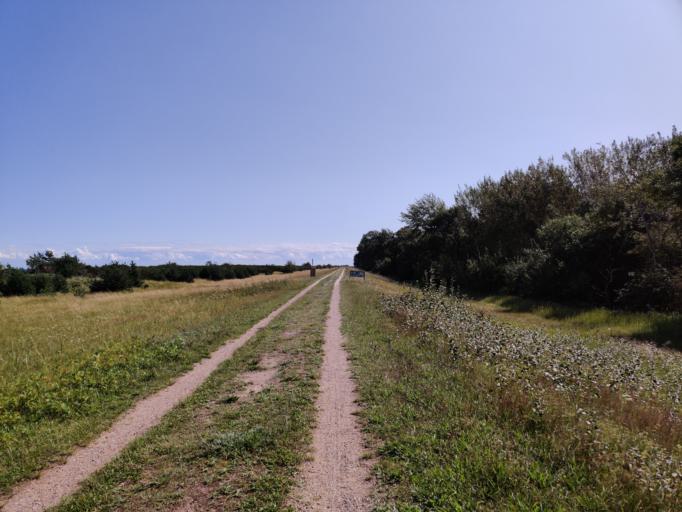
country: DK
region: Zealand
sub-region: Guldborgsund Kommune
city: Nykobing Falster
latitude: 54.6074
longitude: 11.9663
